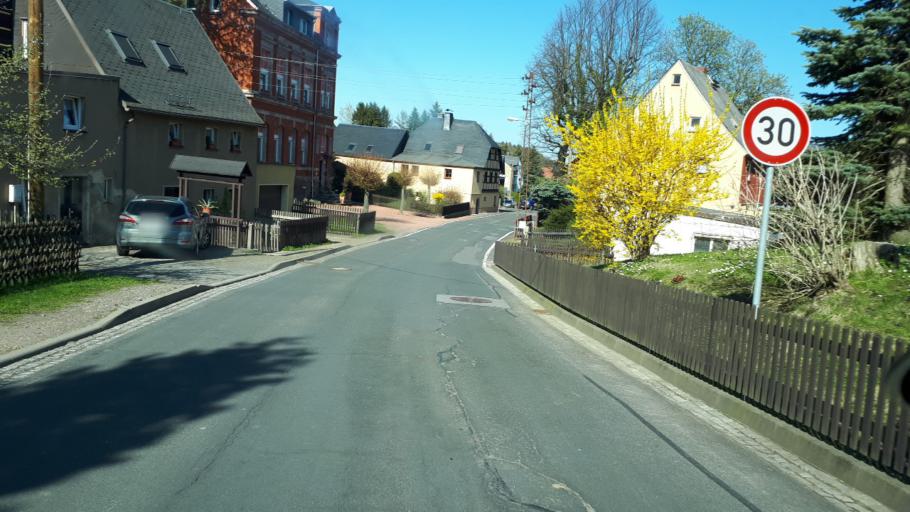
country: DE
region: Saxony
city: Burkhardtsdorf
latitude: 50.7631
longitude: 12.9421
